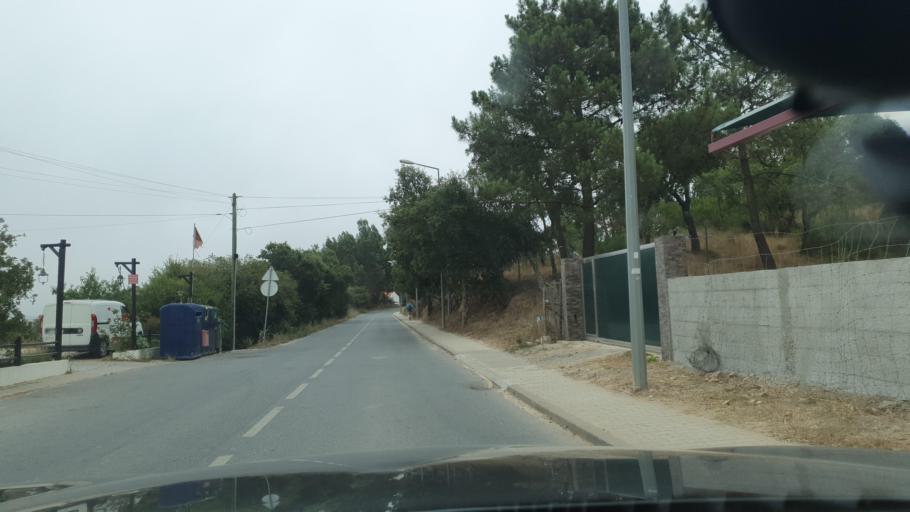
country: PT
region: Beja
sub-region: Odemira
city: Sao Teotonio
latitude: 37.5099
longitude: -8.7137
